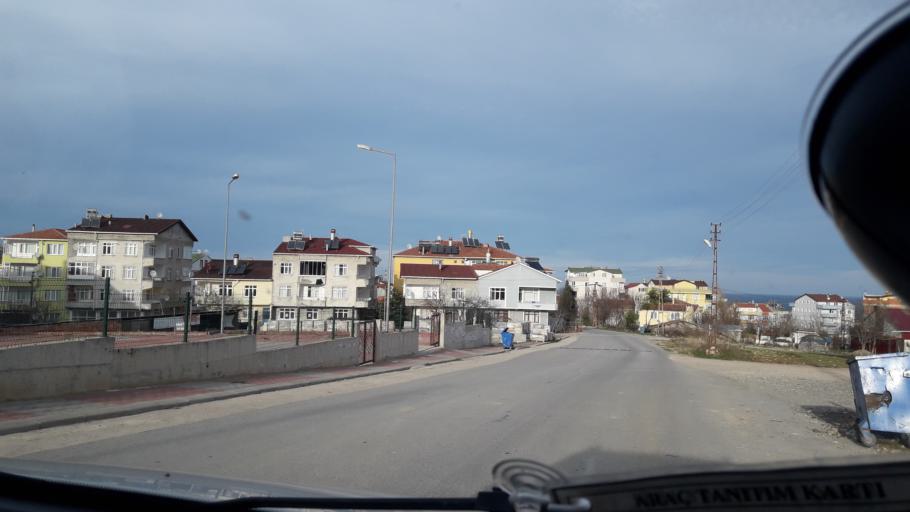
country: TR
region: Sinop
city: Gerze
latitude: 41.8044
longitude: 35.1838
